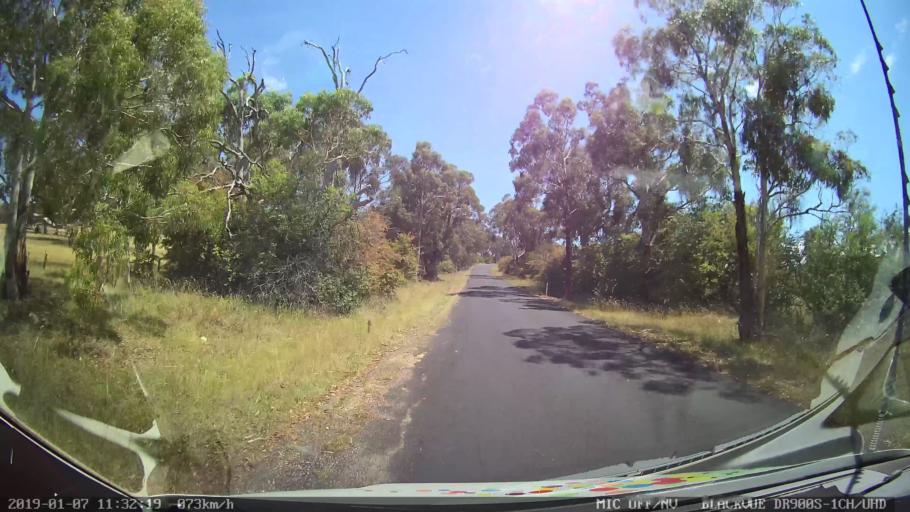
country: AU
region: New South Wales
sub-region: Armidale Dumaresq
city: Armidale
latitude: -30.4103
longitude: 151.5597
